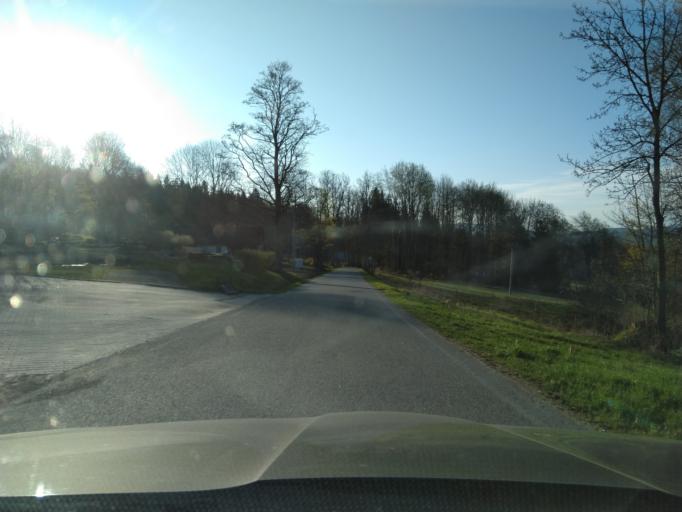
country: DE
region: Bavaria
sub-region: Lower Bavaria
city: Haidmuhle
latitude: 48.8752
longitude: 13.7857
